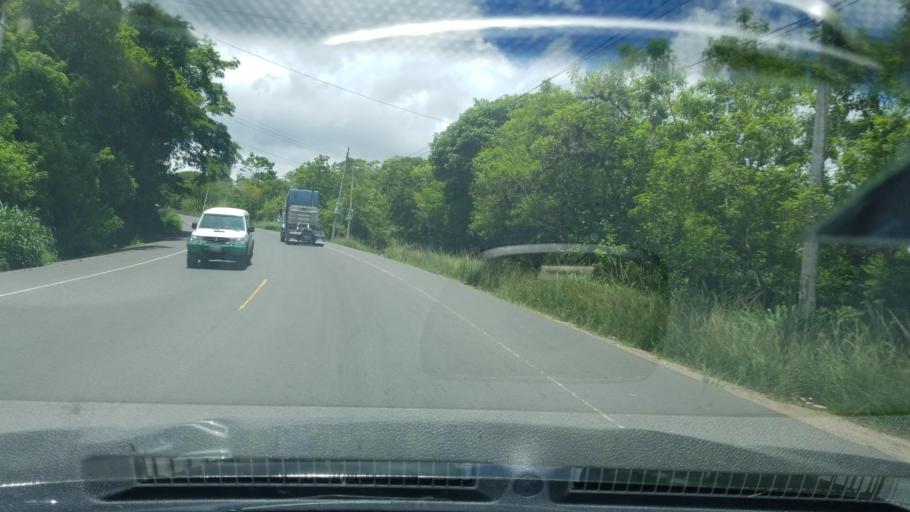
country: HN
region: Francisco Morazan
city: Rio Abajo
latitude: 14.1674
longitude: -87.2053
